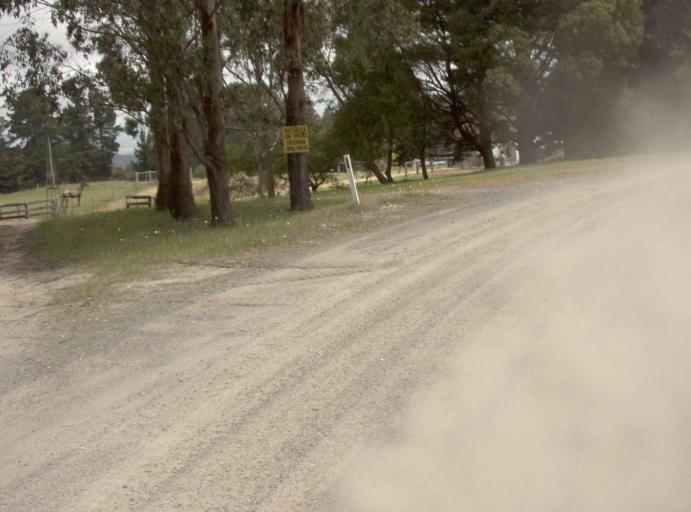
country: AU
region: Victoria
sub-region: Latrobe
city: Traralgon
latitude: -38.4026
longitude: 146.6476
